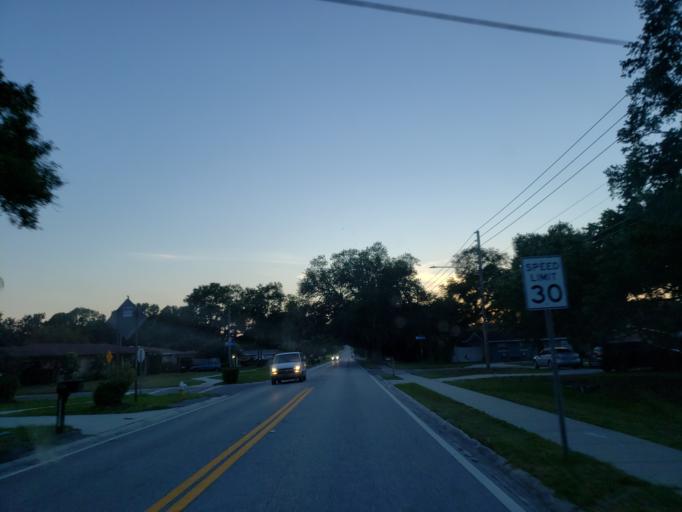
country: US
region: Florida
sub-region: Pinellas County
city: Belleair Bluffs
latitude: 27.9095
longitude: -82.8126
